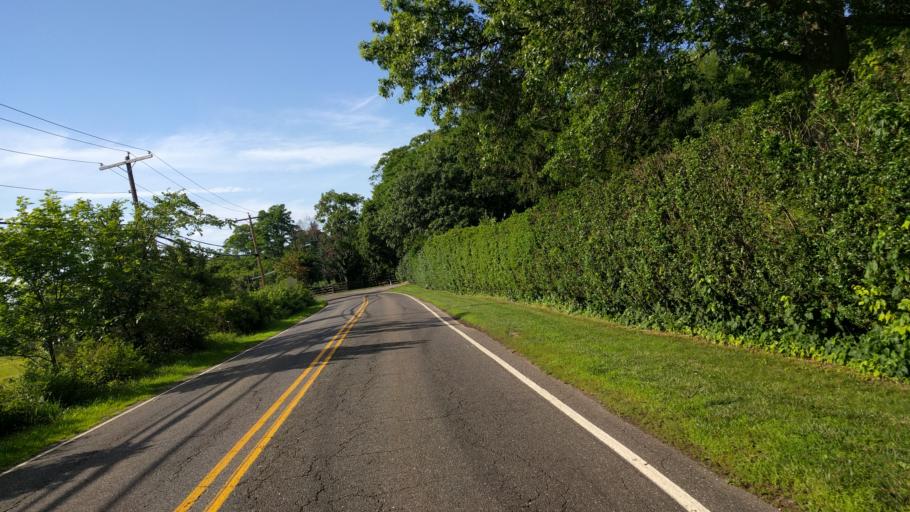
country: US
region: New York
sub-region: Nassau County
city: Oyster Bay Cove
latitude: 40.8730
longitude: -73.5024
